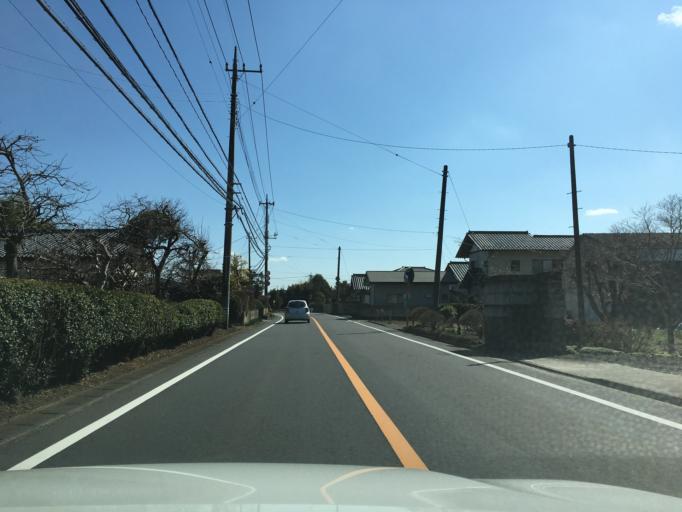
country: JP
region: Tochigi
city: Karasuyama
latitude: 36.7464
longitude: 140.1327
